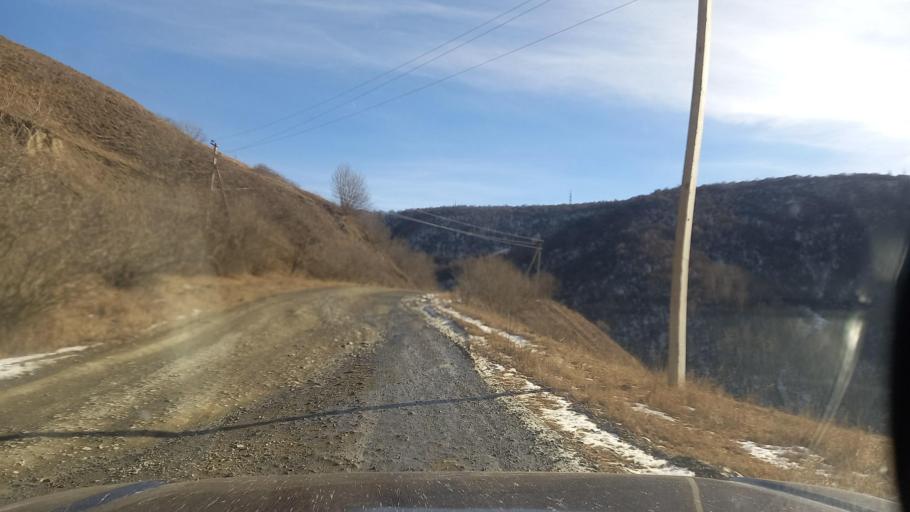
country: RU
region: North Ossetia
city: Verkhniy Fiagdon
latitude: 42.8374
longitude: 44.4671
